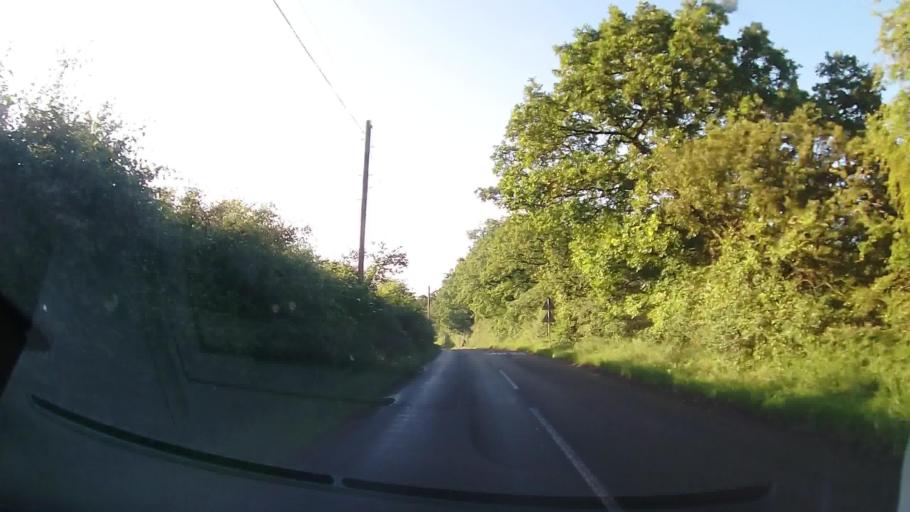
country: GB
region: England
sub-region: Leicestershire
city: Markfield
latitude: 52.6605
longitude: -1.2655
